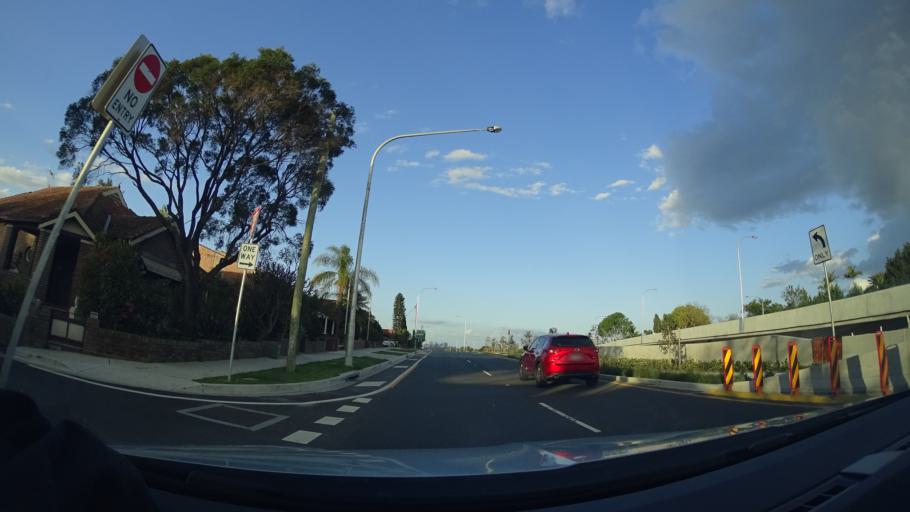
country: AU
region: New South Wales
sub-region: Ashfield
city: Ashfield
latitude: -33.8762
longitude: 151.1319
